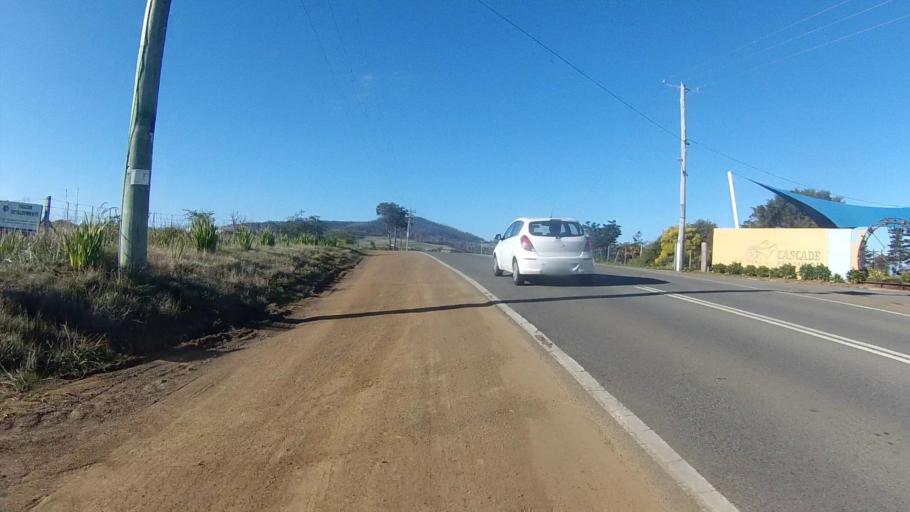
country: AU
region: Tasmania
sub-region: Sorell
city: Sorell
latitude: -42.8920
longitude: 147.8053
